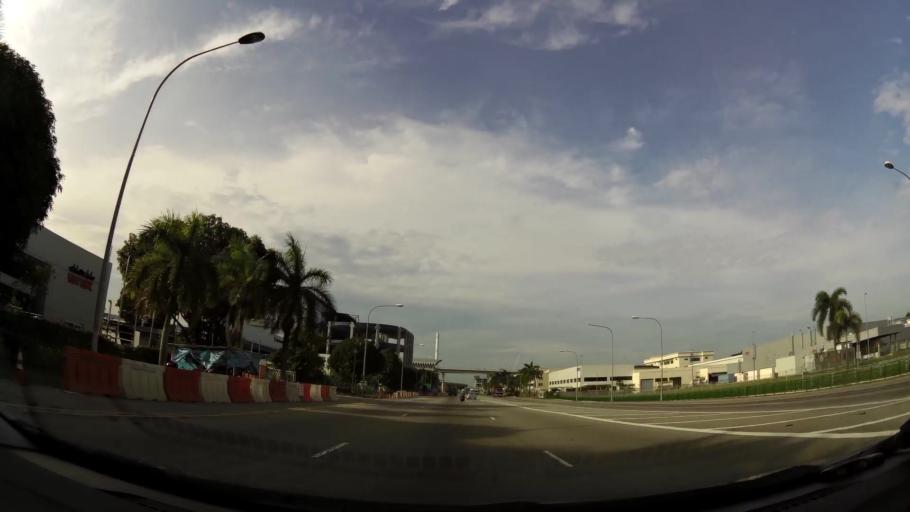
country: MY
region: Johor
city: Johor Bahru
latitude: 1.3334
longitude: 103.6415
